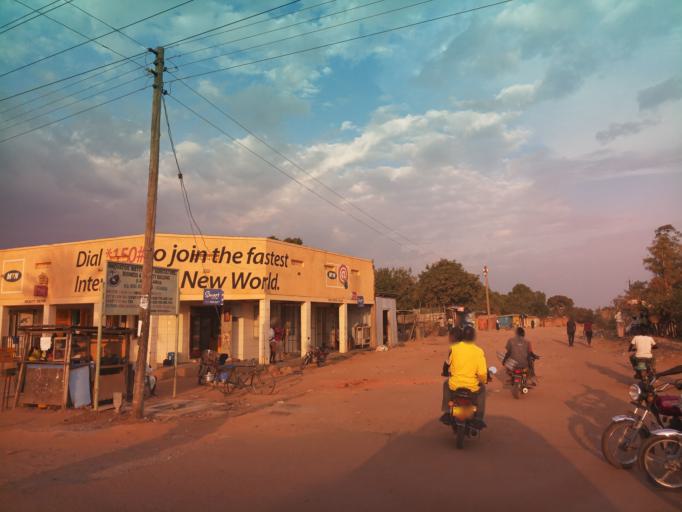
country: UG
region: Northern Region
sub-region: Arua District
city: Arua
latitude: 3.0331
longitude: 30.9134
